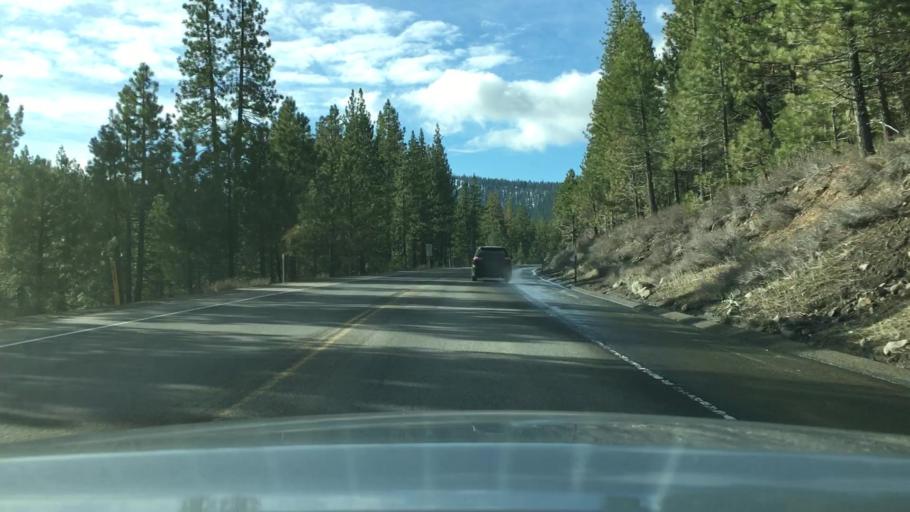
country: US
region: California
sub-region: Placer County
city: Tahoe Vista
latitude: 39.2921
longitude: -120.1036
